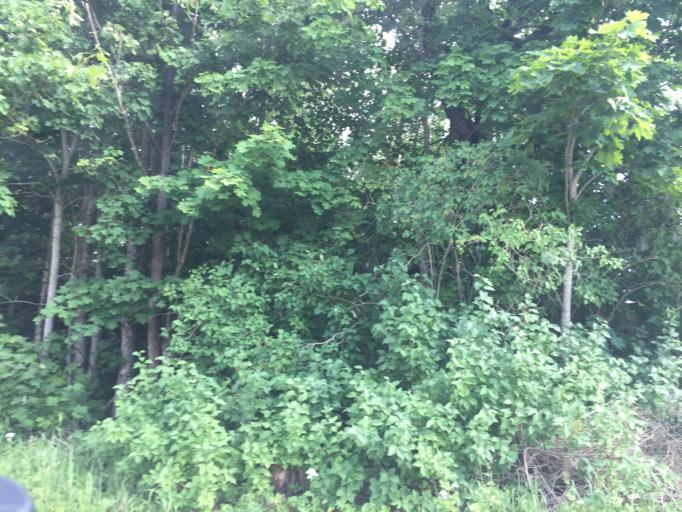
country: LV
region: Skriveri
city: Skriveri
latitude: 56.8367
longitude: 25.1288
